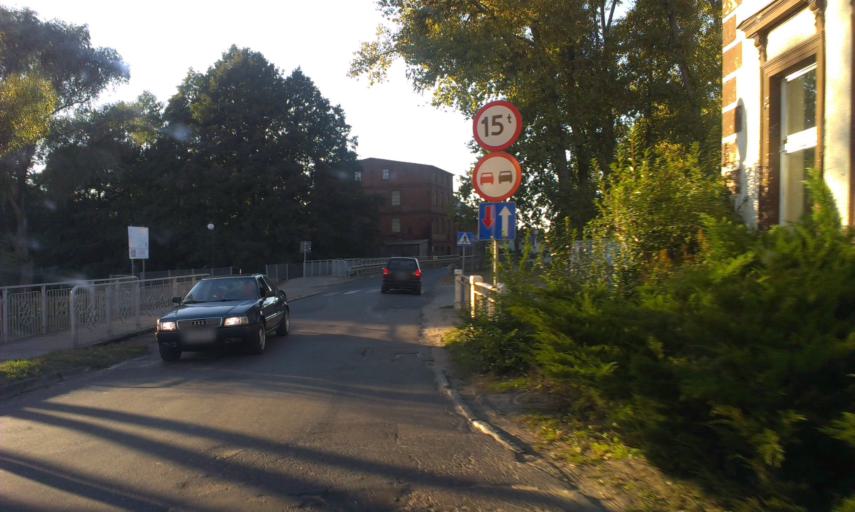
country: PL
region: Pomeranian Voivodeship
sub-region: Powiat czluchowski
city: Czarne
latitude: 53.6842
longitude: 16.9385
